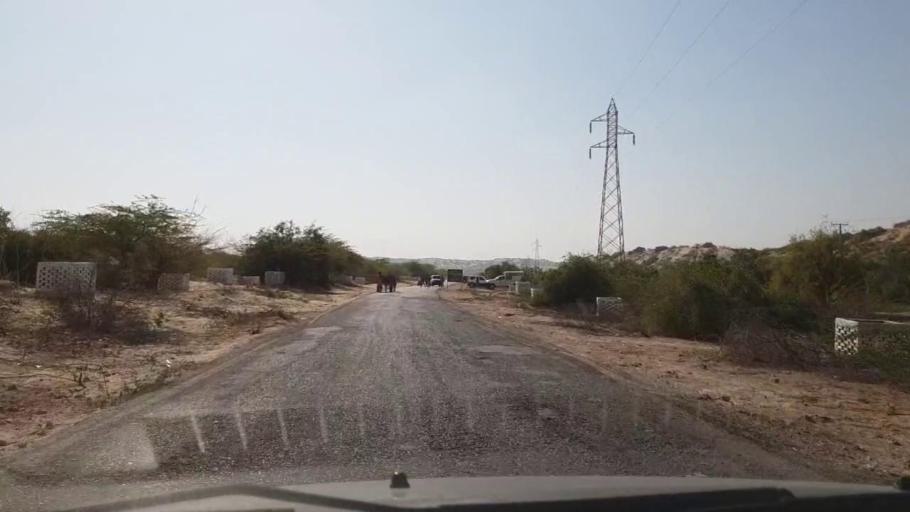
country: PK
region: Sindh
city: Diplo
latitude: 24.4877
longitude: 69.5887
